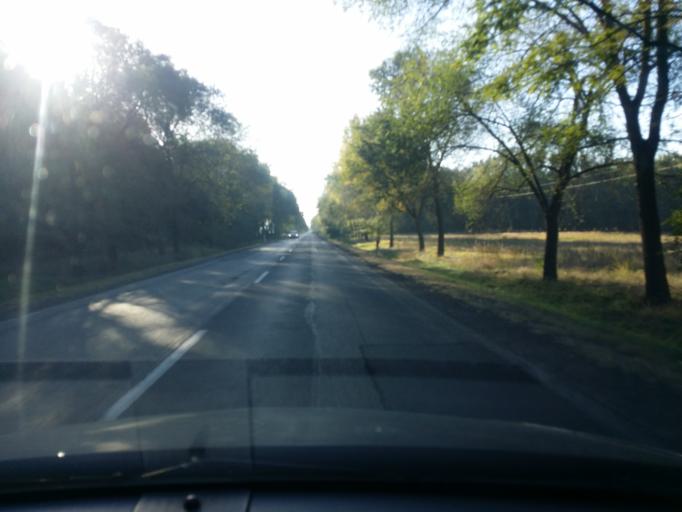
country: HU
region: Bacs-Kiskun
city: Nyarlorinc
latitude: 46.9028
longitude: 19.8162
